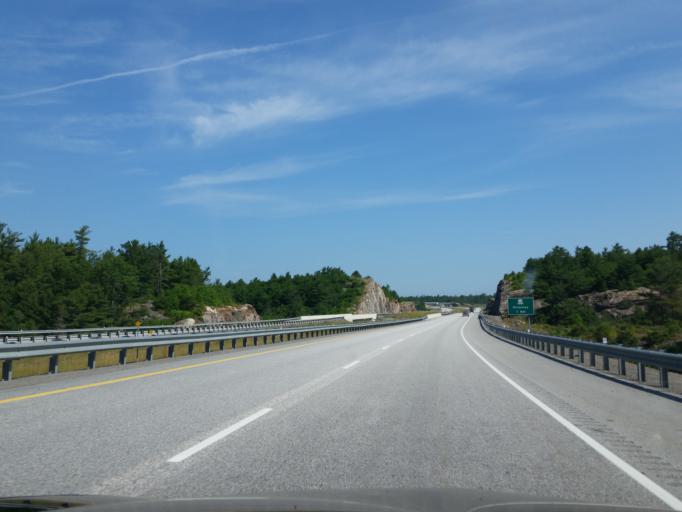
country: CA
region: Ontario
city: Greater Sudbury
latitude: 46.2137
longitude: -80.7693
